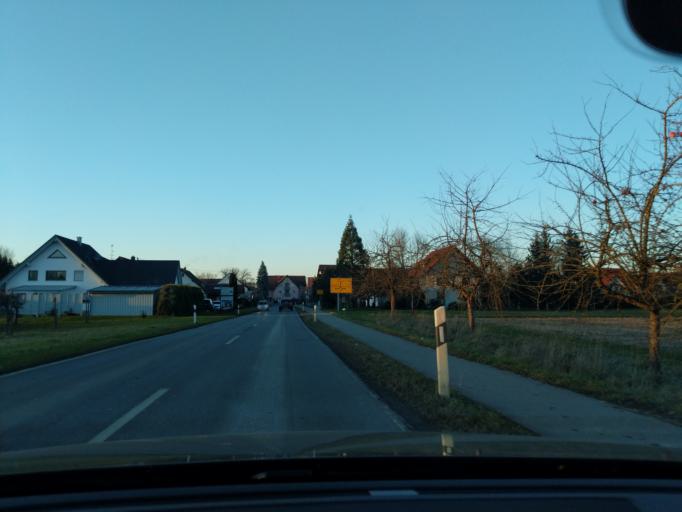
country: DE
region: Baden-Wuerttemberg
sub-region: Tuebingen Region
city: Bermatingen
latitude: 47.7226
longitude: 9.3249
